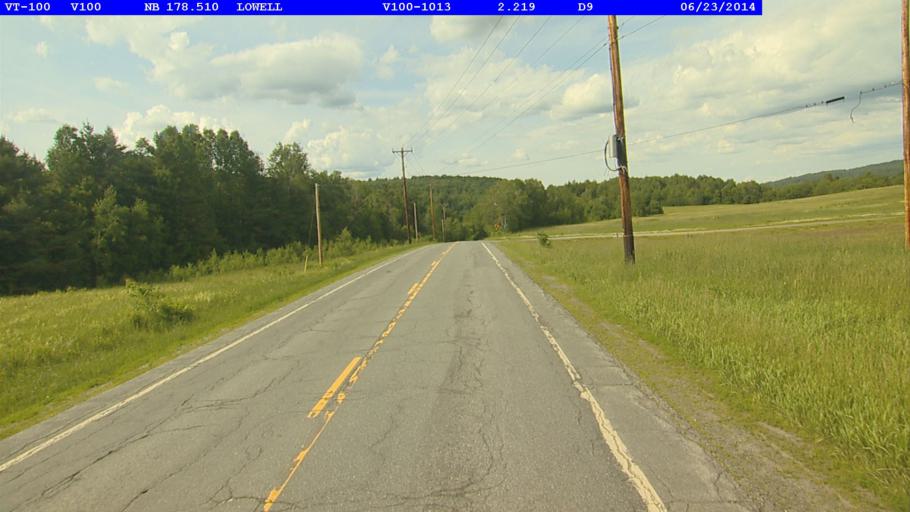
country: US
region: Vermont
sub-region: Lamoille County
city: Hyde Park
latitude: 44.7701
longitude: -72.4572
